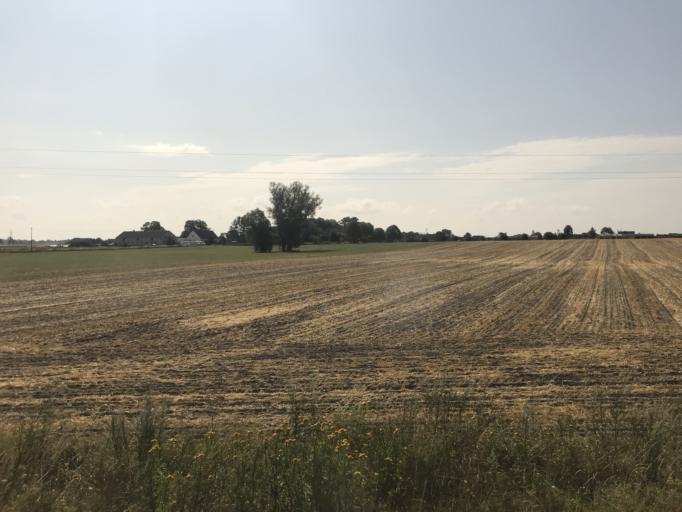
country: PL
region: Kujawsko-Pomorskie
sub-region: Powiat swiecki
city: Pruszcz
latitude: 53.3157
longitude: 18.1695
